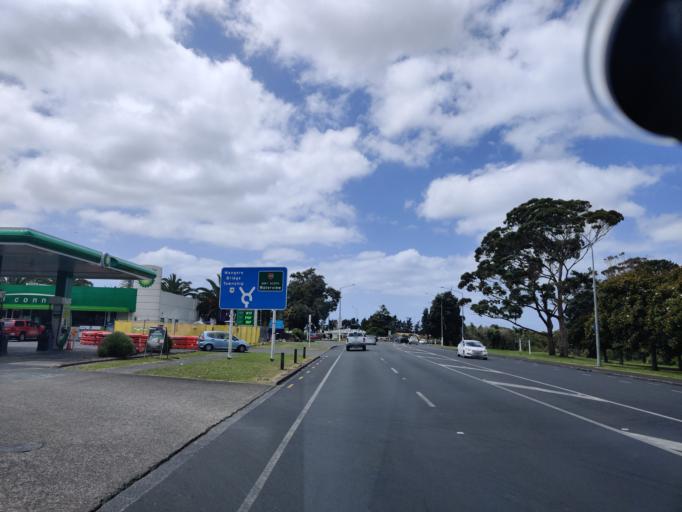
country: NZ
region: Auckland
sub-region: Auckland
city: Mangere
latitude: -36.9541
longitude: 174.7910
